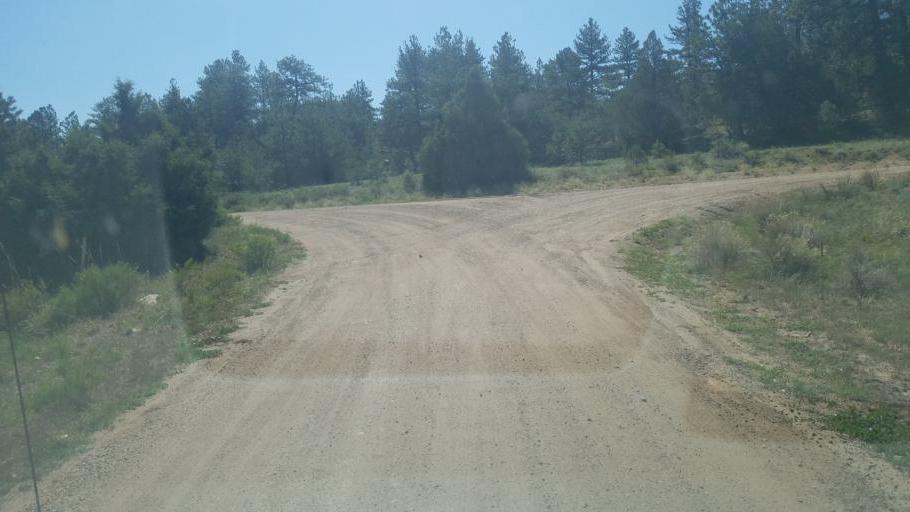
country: US
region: Colorado
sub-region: Custer County
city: Westcliffe
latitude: 38.2872
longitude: -105.4497
